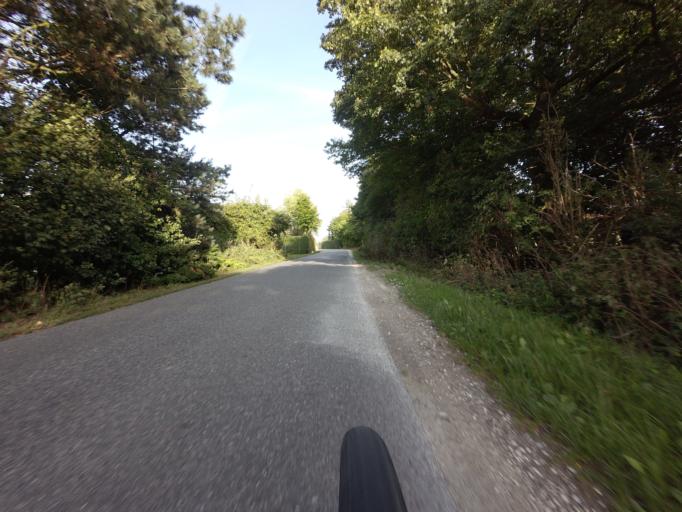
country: DK
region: Zealand
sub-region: Faxe Kommune
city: Fakse Ladeplads
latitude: 55.2514
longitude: 12.2522
